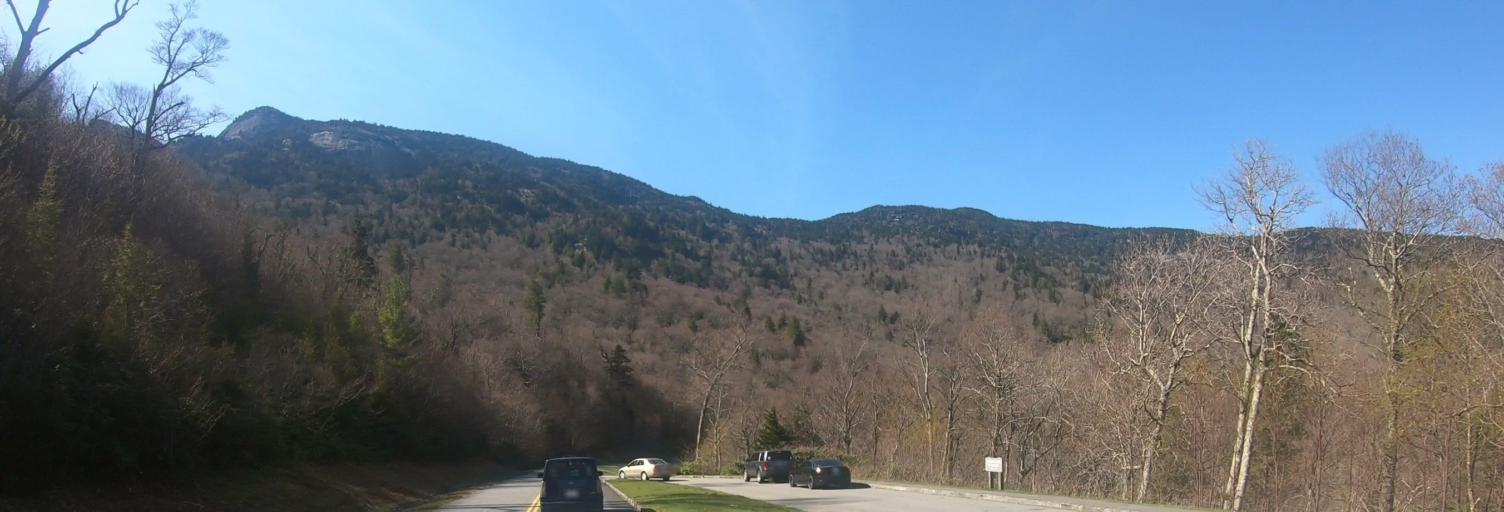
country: US
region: North Carolina
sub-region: Watauga County
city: Foscoe
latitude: 36.0965
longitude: -81.8113
